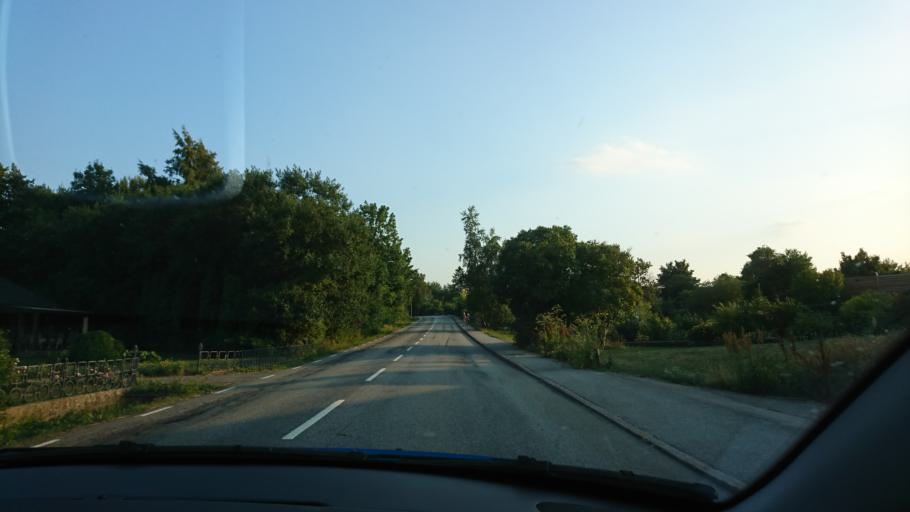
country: SE
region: Skane
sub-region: Simrishamns Kommun
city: Kivik
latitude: 55.6886
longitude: 14.1556
